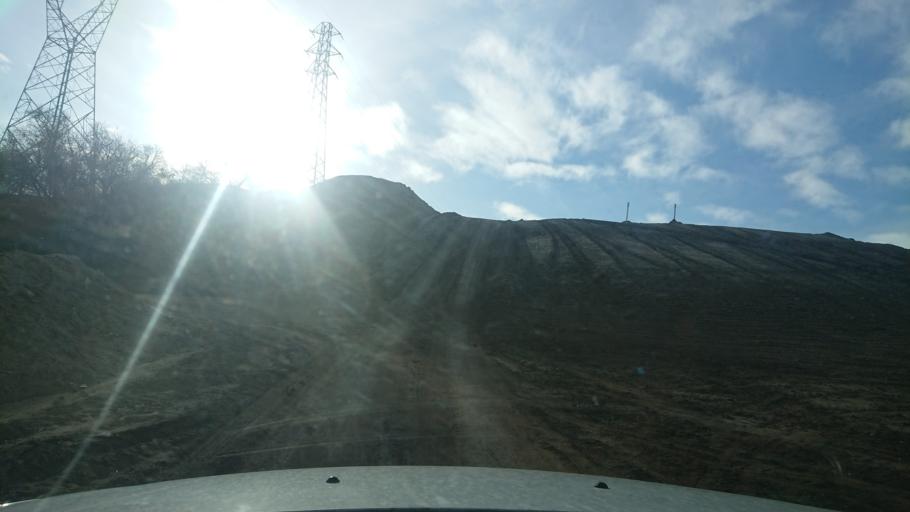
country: TR
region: Aksaray
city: Agacoren
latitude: 38.8592
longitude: 33.9427
